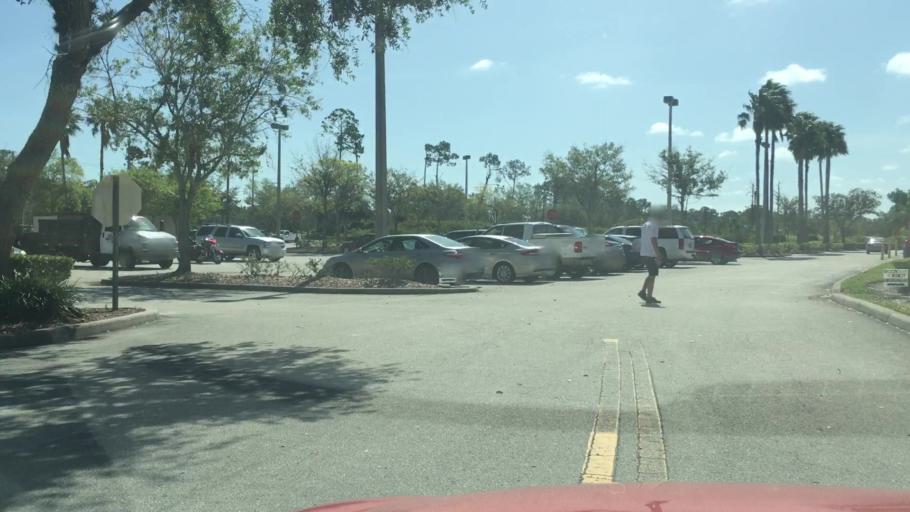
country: US
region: Florida
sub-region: Volusia County
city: South Daytona
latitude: 29.1428
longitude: -81.0366
